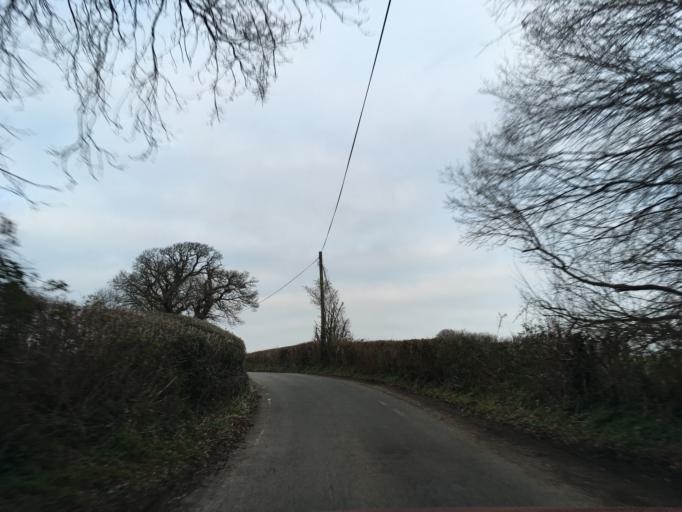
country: GB
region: Wales
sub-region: Newport
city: Marshfield
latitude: 51.5651
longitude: -3.0825
